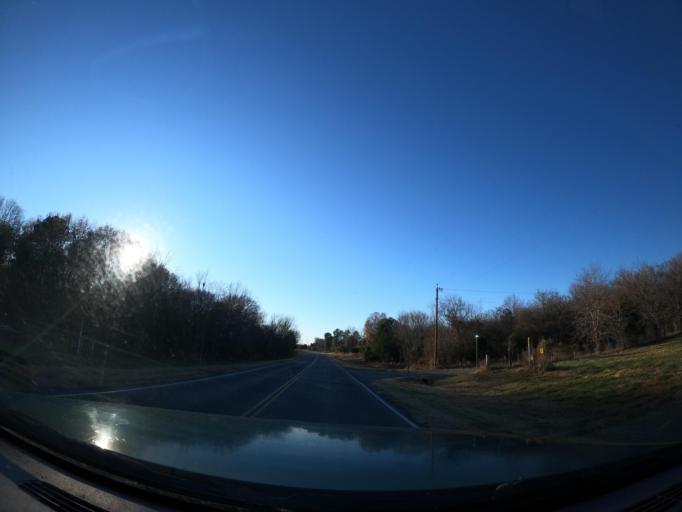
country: US
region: Oklahoma
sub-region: Pittsburg County
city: Hartshorne
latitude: 34.8875
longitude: -95.4776
